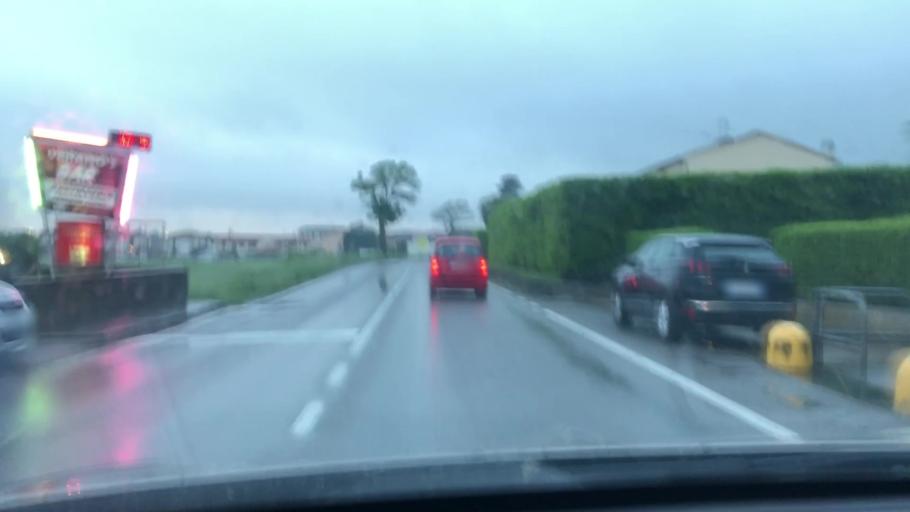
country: IT
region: Tuscany
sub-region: Province of Pisa
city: Val di Cava
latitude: 43.6385
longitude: 10.6520
